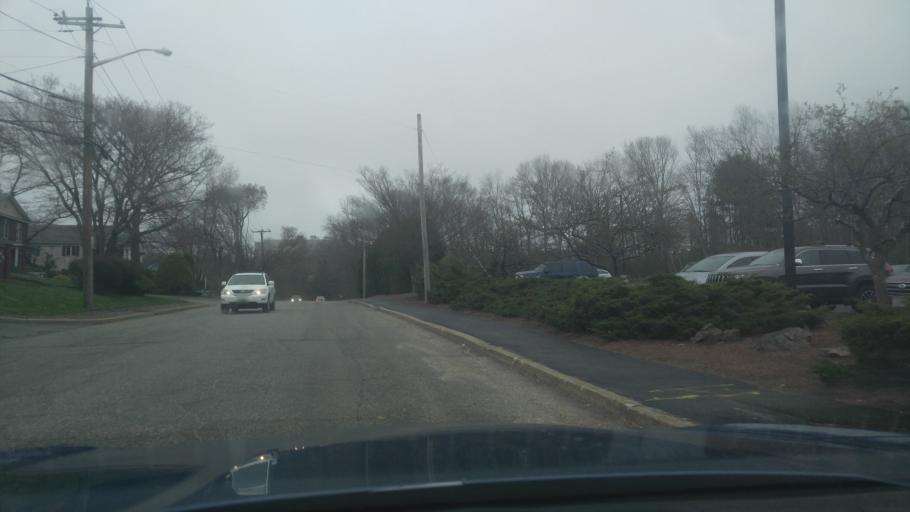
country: US
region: Rhode Island
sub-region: Kent County
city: West Warwick
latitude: 41.7135
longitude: -71.4871
